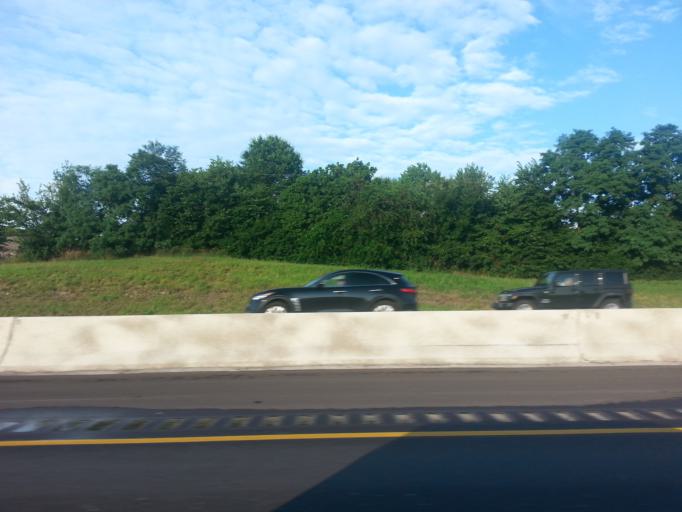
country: US
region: Kentucky
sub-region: Madison County
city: Richmond
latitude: 37.7037
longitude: -84.3187
